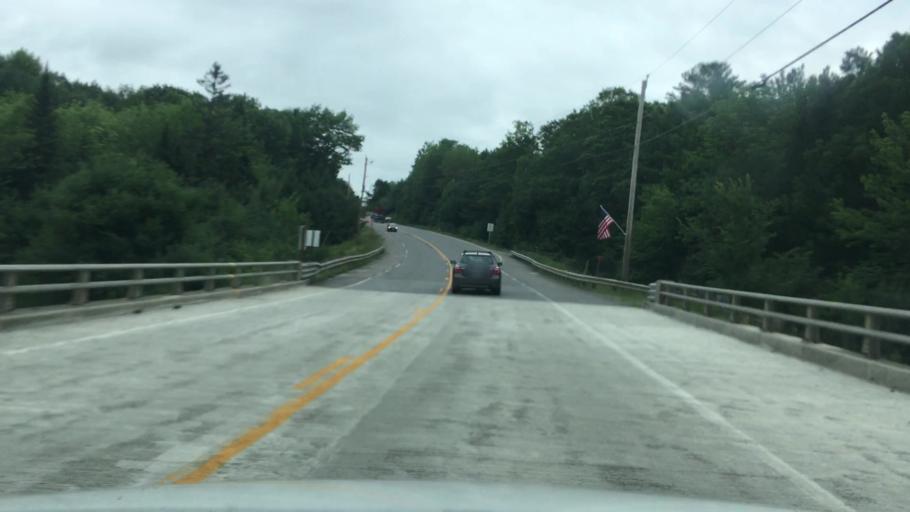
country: US
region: Maine
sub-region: Penobscot County
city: Bradley
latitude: 44.8273
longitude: -68.3756
